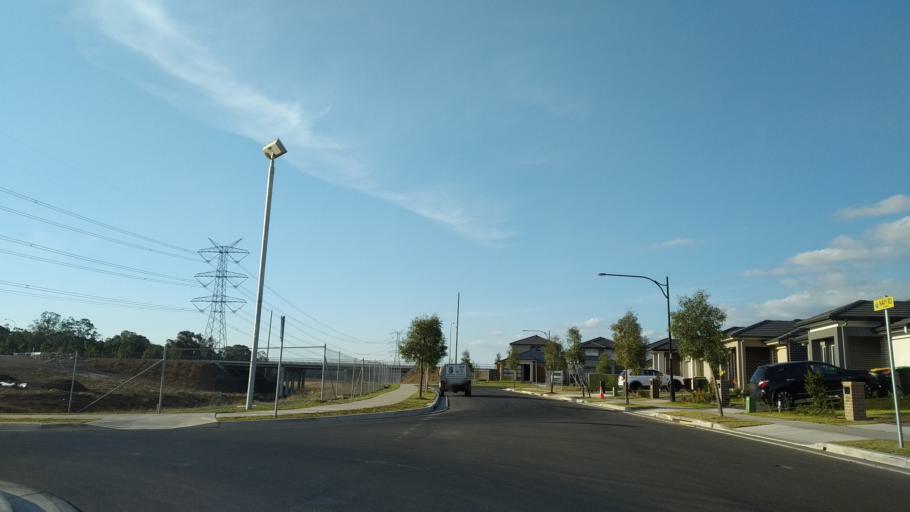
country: AU
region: New South Wales
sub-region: Penrith Municipality
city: Werrington County
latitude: -33.7361
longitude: 150.7510
